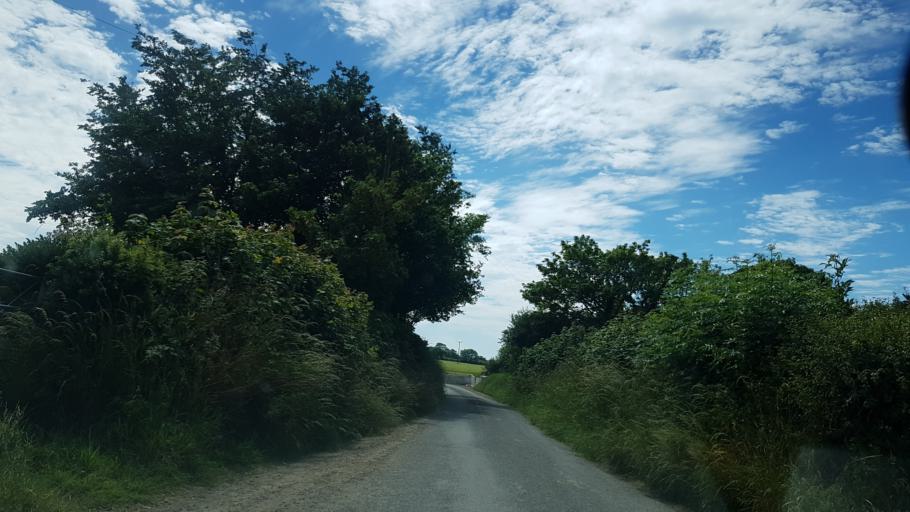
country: GB
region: Wales
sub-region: Pembrokeshire
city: Wiston
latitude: 51.8243
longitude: -4.9130
